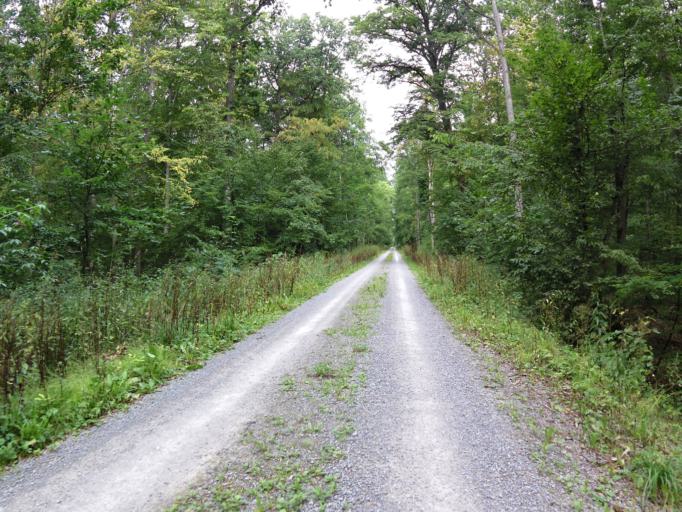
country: DE
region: Bavaria
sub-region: Regierungsbezirk Unterfranken
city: Kist
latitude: 49.7240
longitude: 9.8299
